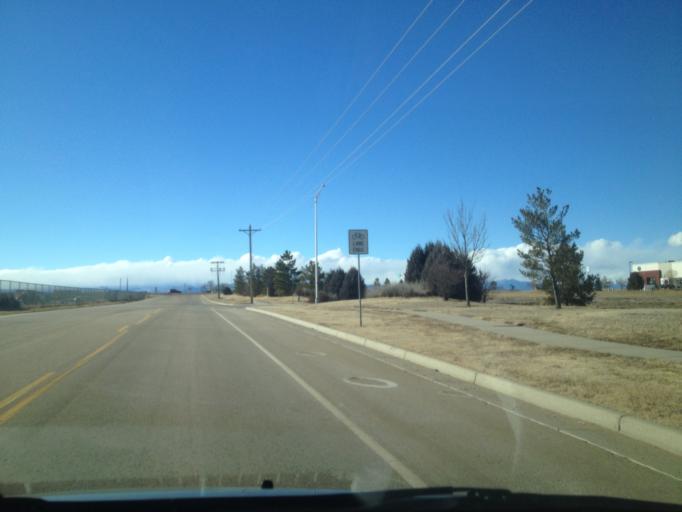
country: US
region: Colorado
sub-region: Weld County
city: Dacono
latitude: 40.0731
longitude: -104.9772
